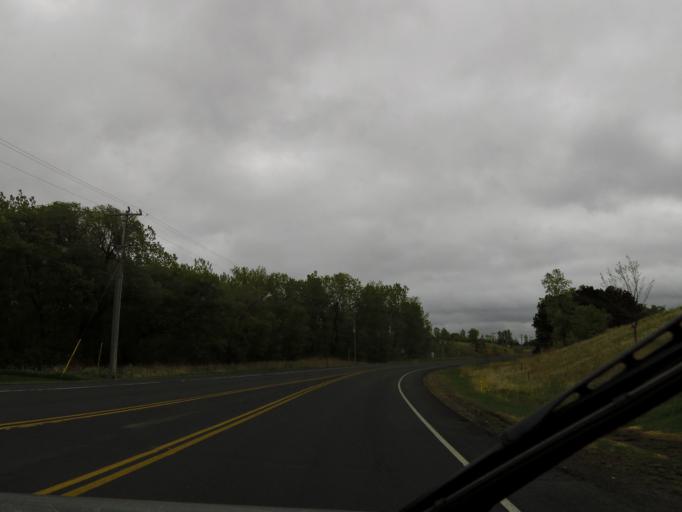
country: US
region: Minnesota
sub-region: Washington County
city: Oakdale
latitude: 44.9522
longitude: -92.9298
